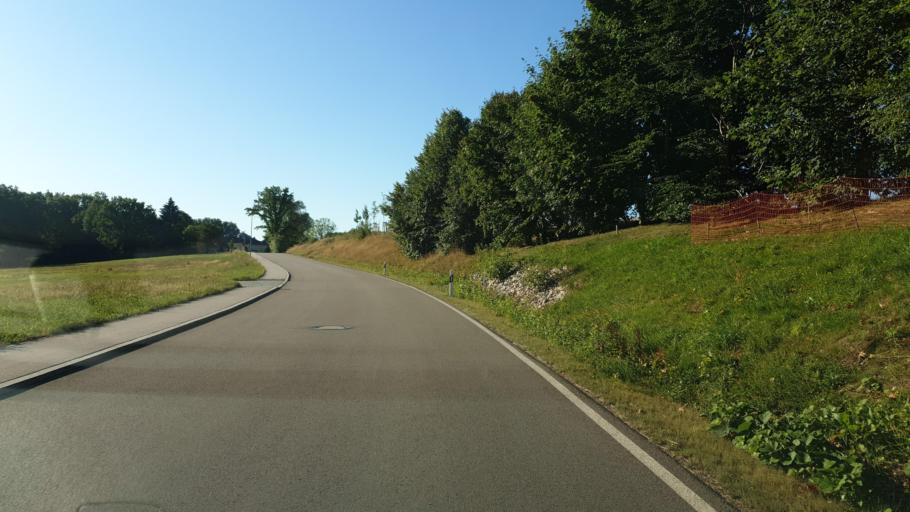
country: DE
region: Saxony
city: Lichtentanne
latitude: 50.6679
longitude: 12.4335
